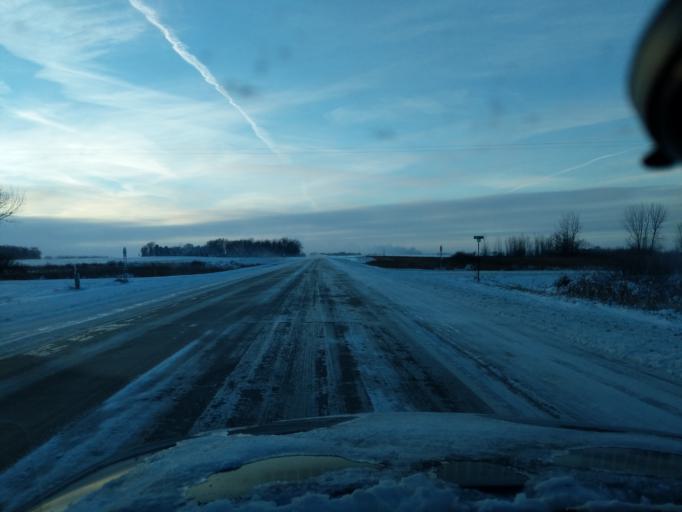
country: US
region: Minnesota
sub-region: Renville County
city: Renville
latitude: 44.7891
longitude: -95.1171
